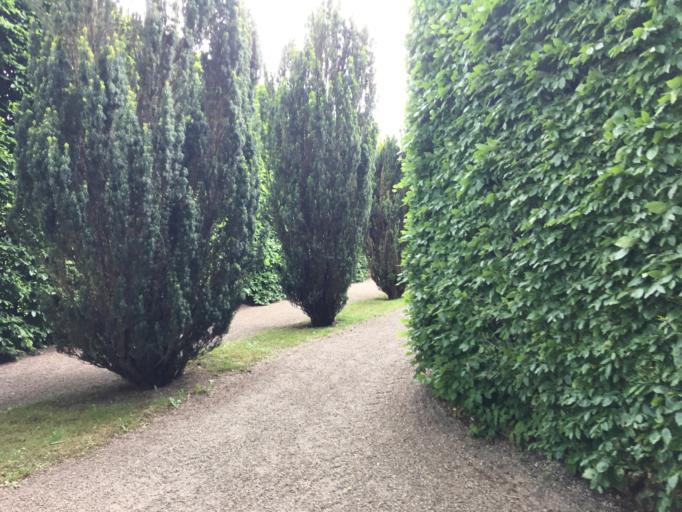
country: DK
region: South Denmark
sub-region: Faaborg-Midtfyn Kommune
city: Ringe
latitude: 55.1767
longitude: 10.4911
